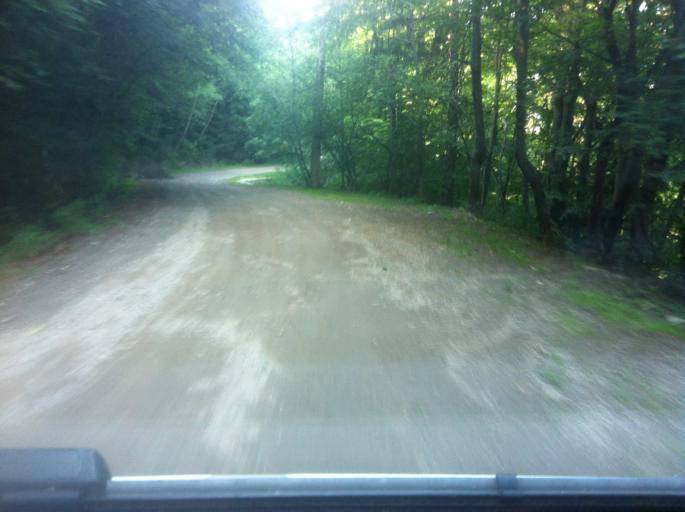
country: RO
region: Hunedoara
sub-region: Comuna Rau de Mori
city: Rau de Mori
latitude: 45.4378
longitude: 22.8923
